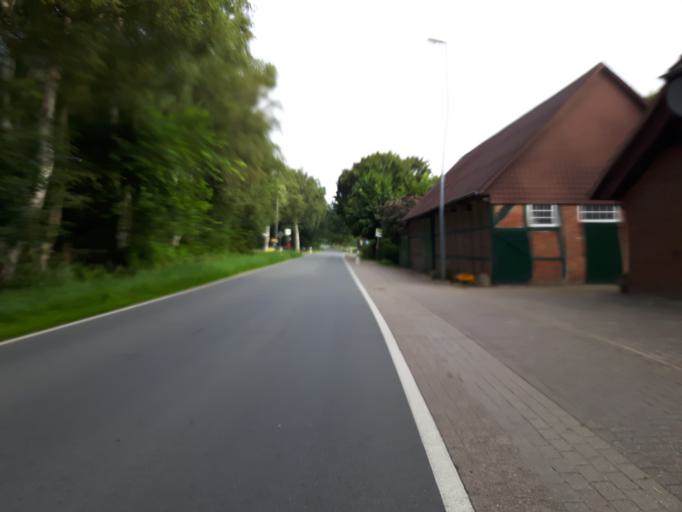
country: DE
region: Lower Saxony
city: Delmenhorst
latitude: 53.0928
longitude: 8.6023
